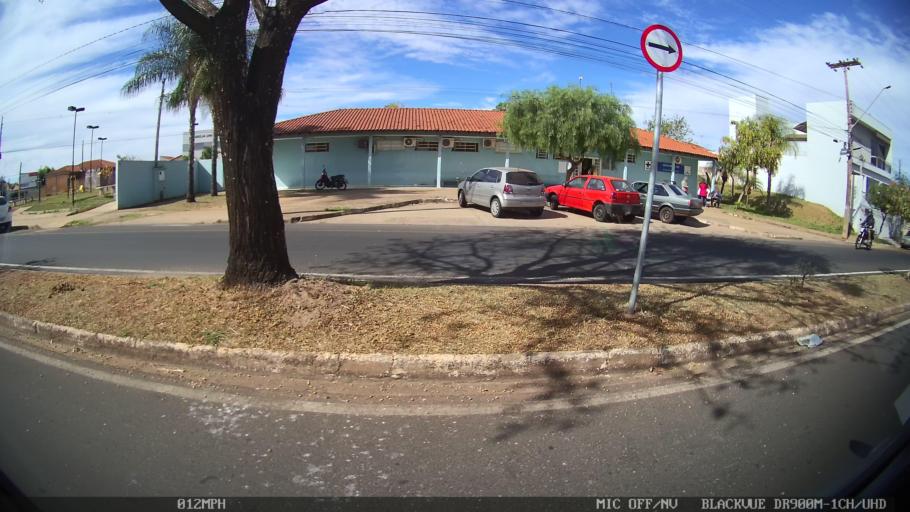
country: BR
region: Sao Paulo
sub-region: Catanduva
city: Catanduva
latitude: -21.1244
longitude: -48.9474
